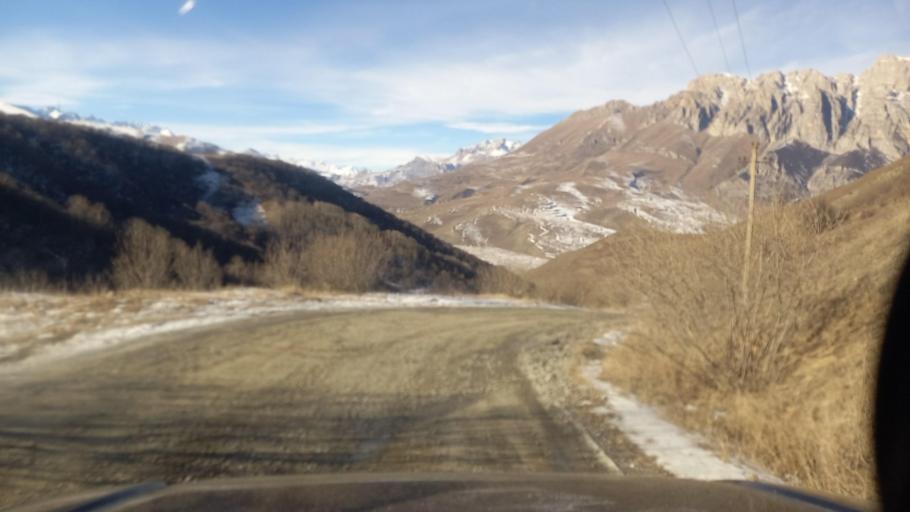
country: RU
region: North Ossetia
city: Verkhniy Fiagdon
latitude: 42.8352
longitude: 44.4727
